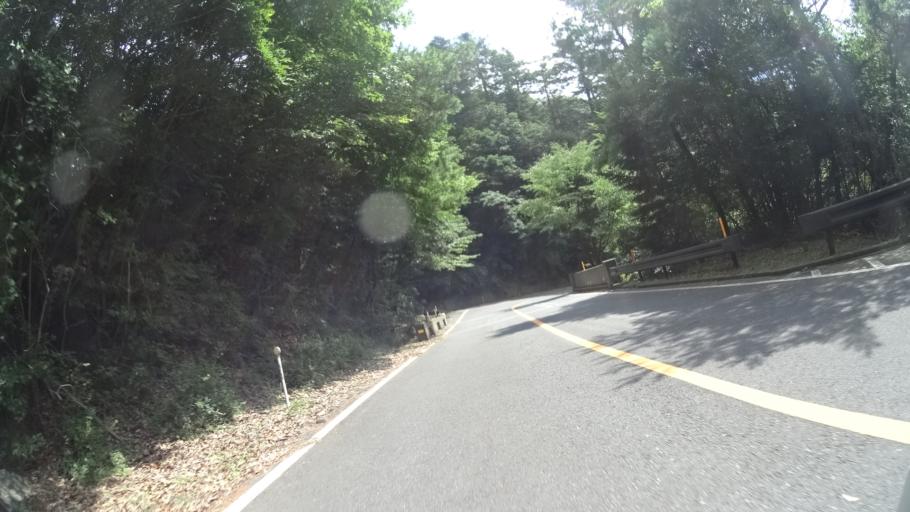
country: JP
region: Miyazaki
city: Kobayashi
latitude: 31.9033
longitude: 130.8442
